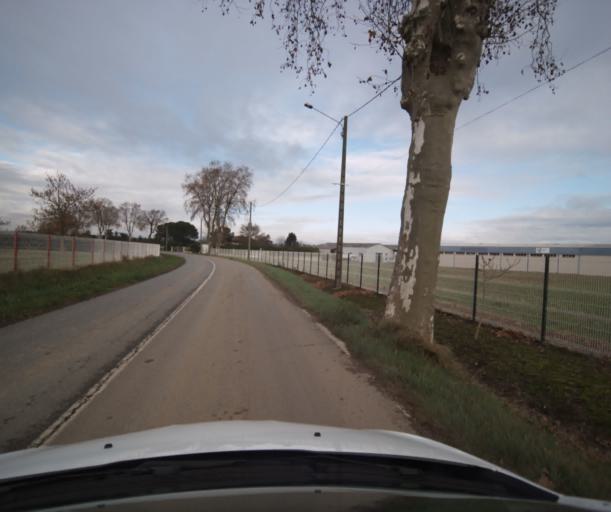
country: FR
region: Midi-Pyrenees
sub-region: Departement de la Haute-Garonne
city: Saint-Alban
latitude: 43.7087
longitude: 1.4075
